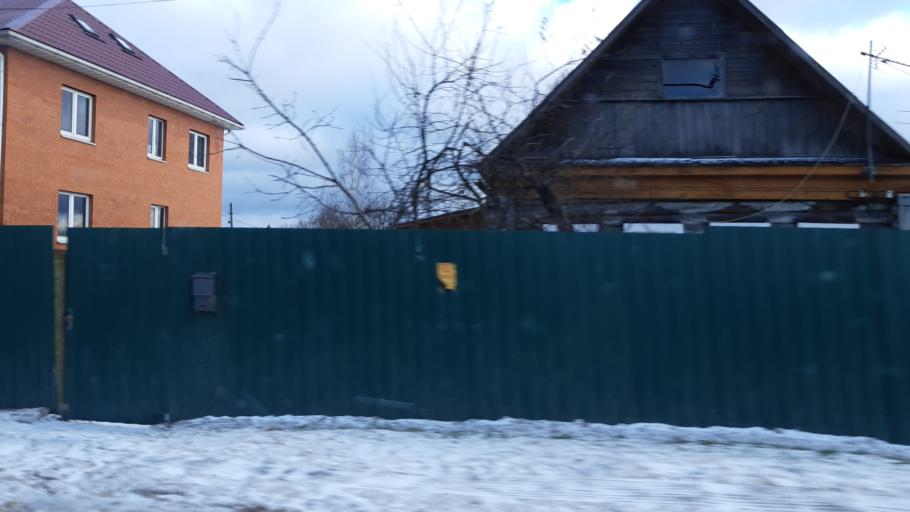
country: RU
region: Moskovskaya
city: Noginsk-9
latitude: 55.9896
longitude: 38.5424
